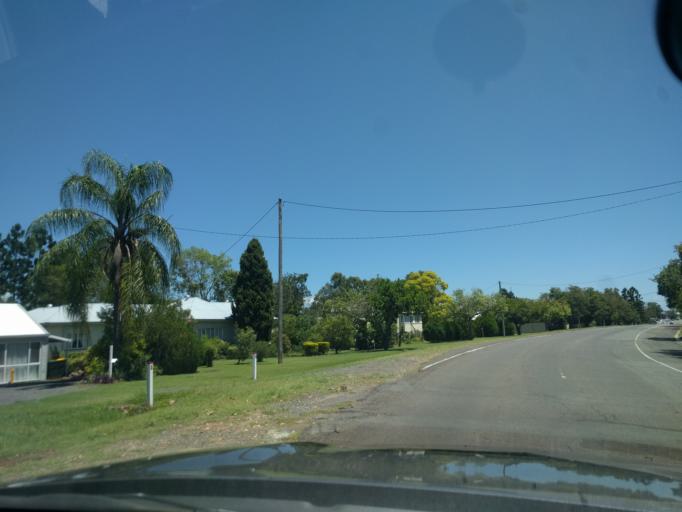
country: AU
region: Queensland
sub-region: Logan
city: Cedar Vale
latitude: -27.9945
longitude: 152.9967
